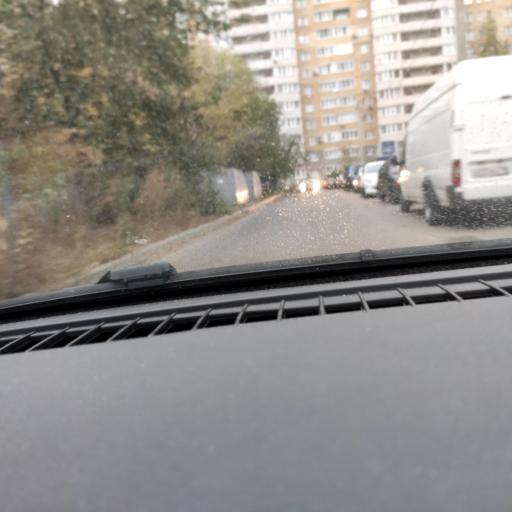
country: RU
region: Voronezj
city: Voronezh
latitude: 51.6481
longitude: 39.2356
